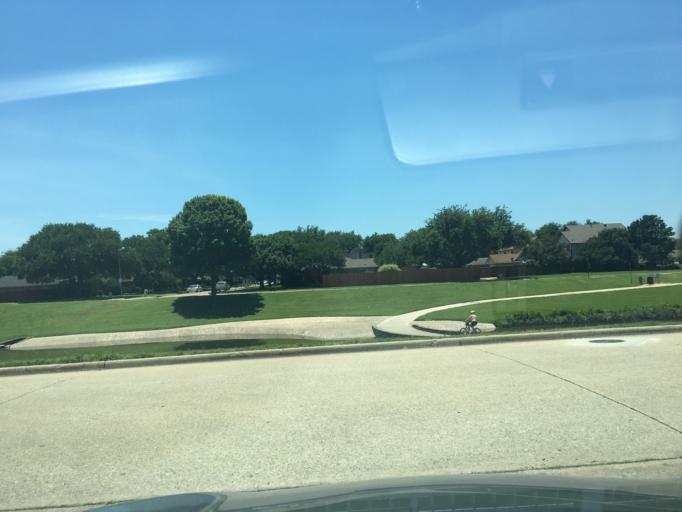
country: US
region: Texas
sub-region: Dallas County
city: Richardson
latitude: 32.9510
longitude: -96.6877
